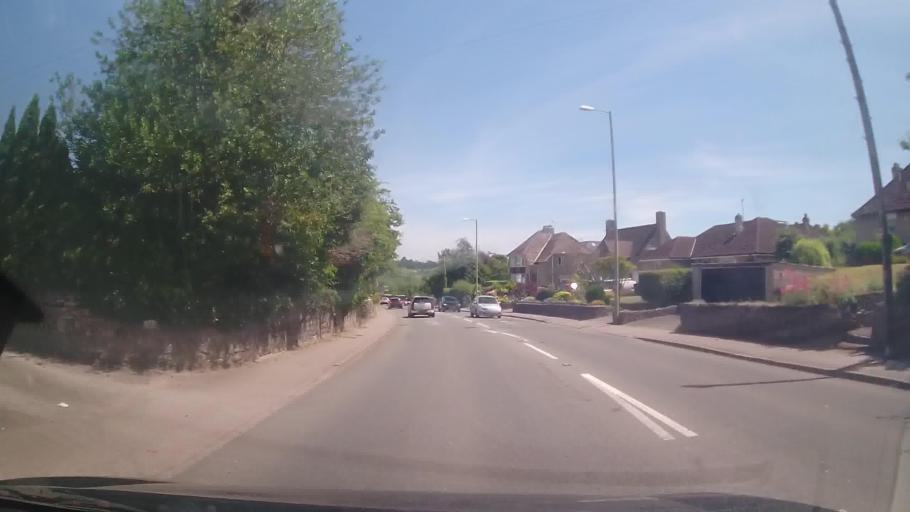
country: GB
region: England
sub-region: Bath and North East Somerset
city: Saltford
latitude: 51.4008
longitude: -2.4548
